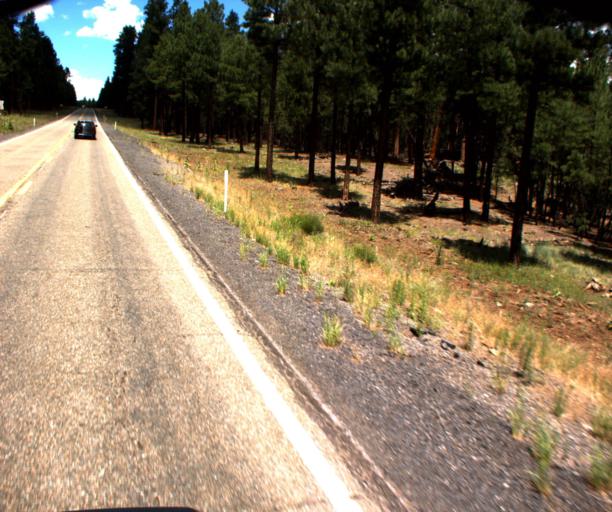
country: US
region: Arizona
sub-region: Coconino County
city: Flagstaff
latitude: 35.2714
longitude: -111.7431
